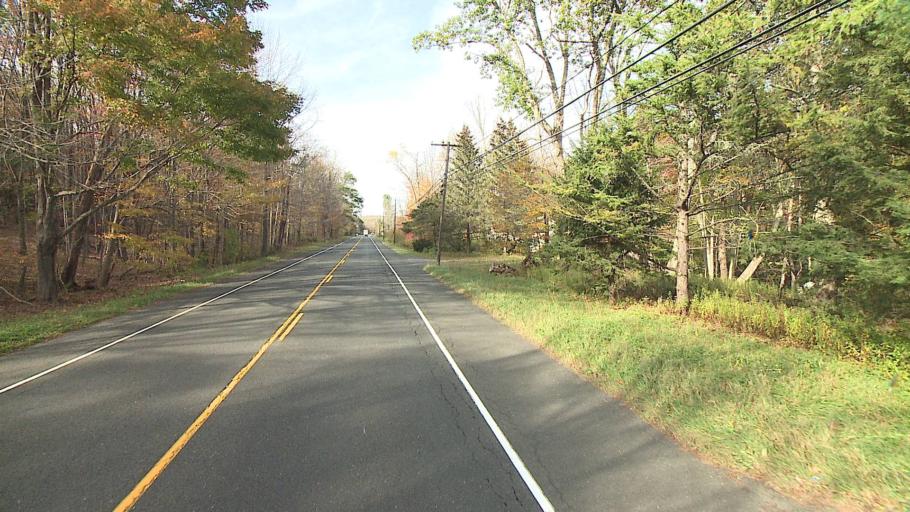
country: US
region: Connecticut
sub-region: Litchfield County
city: Winchester Center
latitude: 41.9531
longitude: -73.1156
